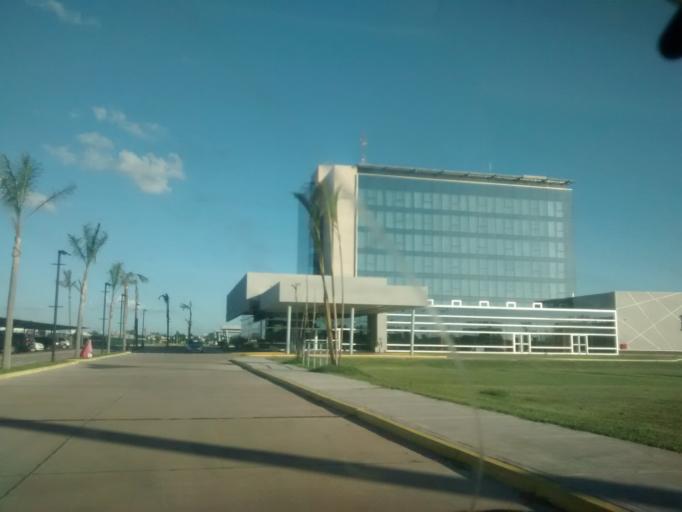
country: AR
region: Chaco
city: Fontana
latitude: -27.4465
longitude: -59.0228
